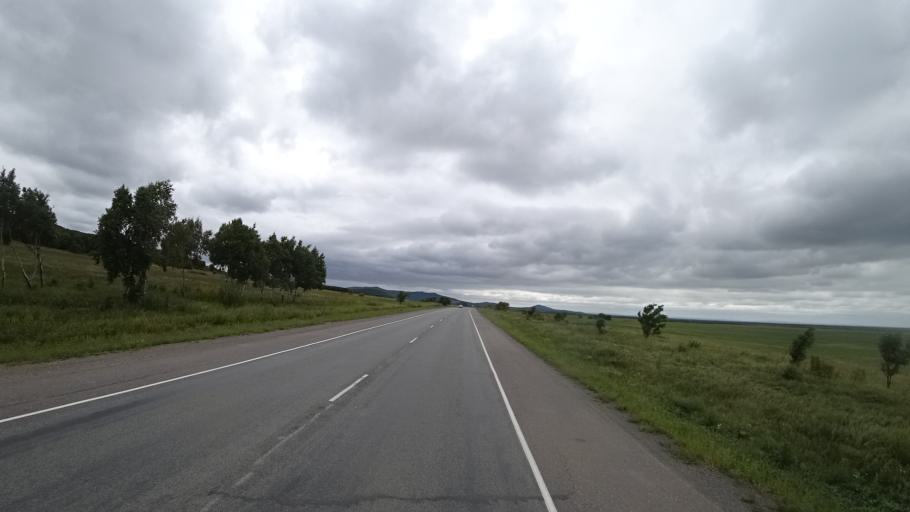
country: RU
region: Primorskiy
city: Chernigovka
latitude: 44.3047
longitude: 132.5365
